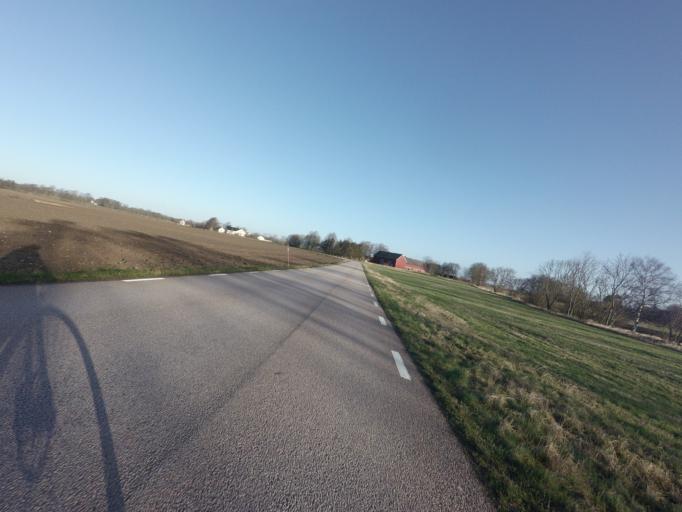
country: SE
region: Skane
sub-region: Helsingborg
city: Odakra
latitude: 56.1120
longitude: 12.6825
